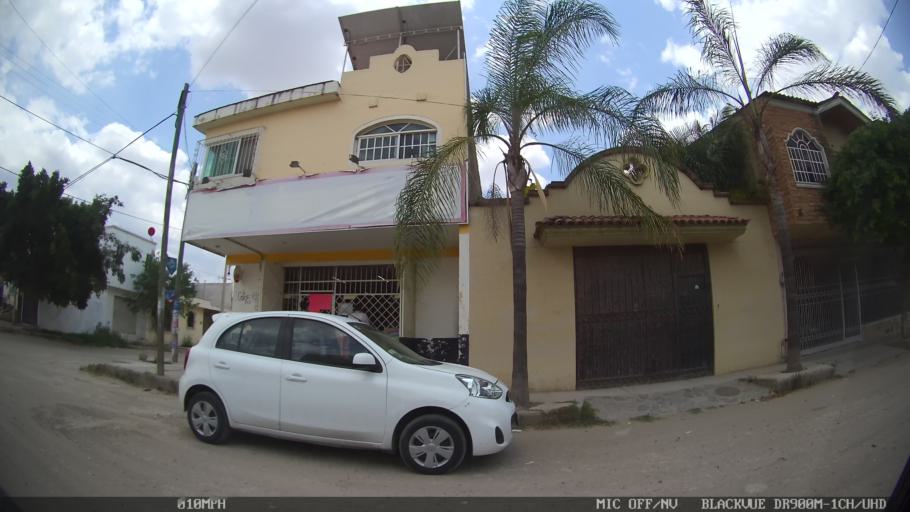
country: MX
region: Jalisco
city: Tonala
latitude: 20.6552
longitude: -103.2277
